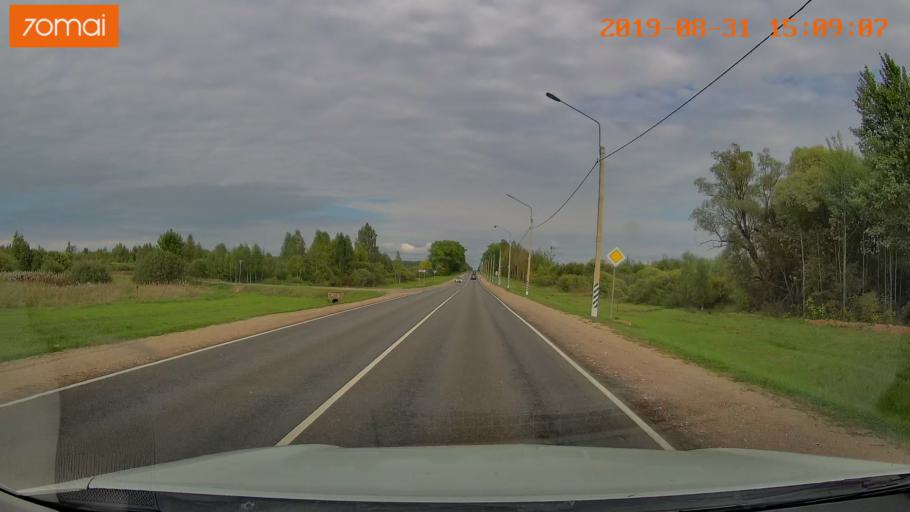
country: RU
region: Kaluga
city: Spas-Demensk
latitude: 54.3983
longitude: 34.1948
